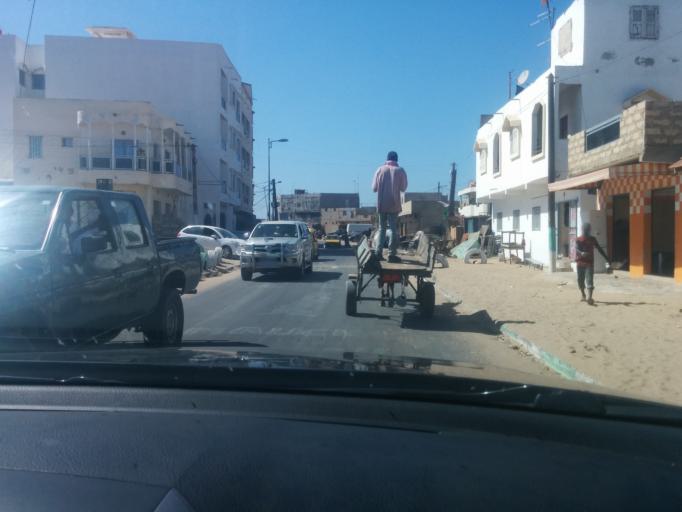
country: SN
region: Dakar
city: Grand Dakar
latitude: 14.7400
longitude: -17.4417
